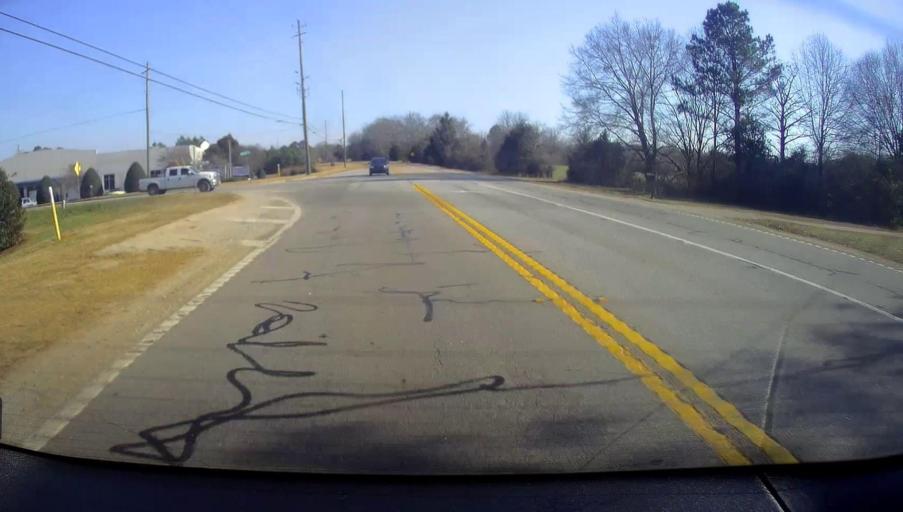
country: US
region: Georgia
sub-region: Henry County
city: Locust Grove
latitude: 33.3231
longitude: -84.0619
